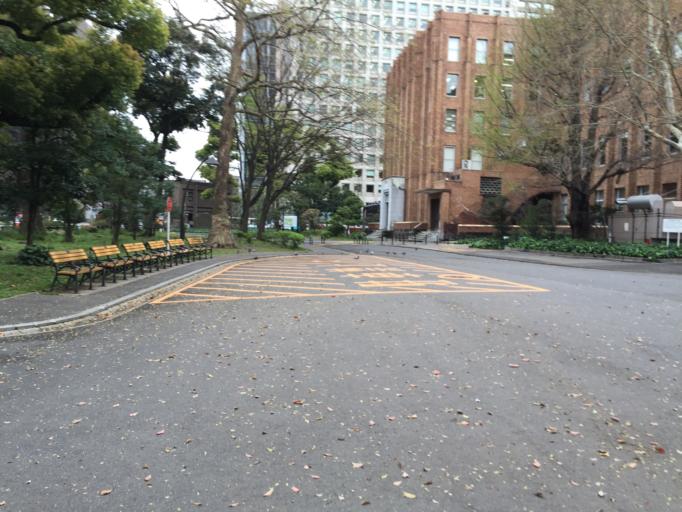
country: JP
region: Tokyo
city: Tokyo
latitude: 35.6717
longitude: 139.7564
